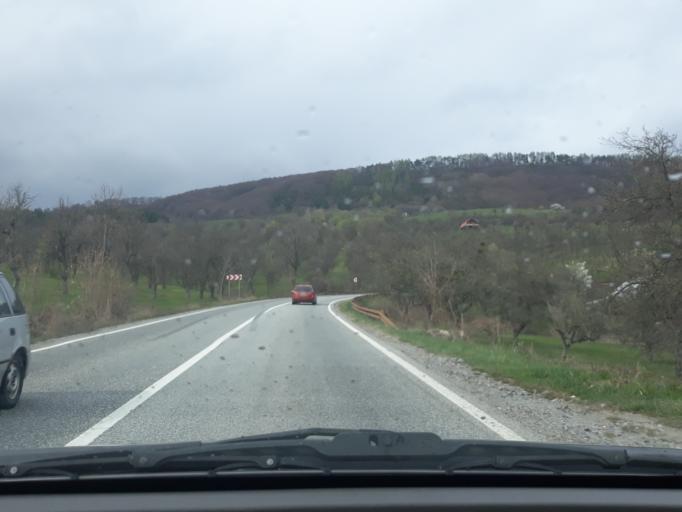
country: RO
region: Harghita
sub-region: Comuna Lupeni
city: Lupeni
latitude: 46.4068
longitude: 25.2126
